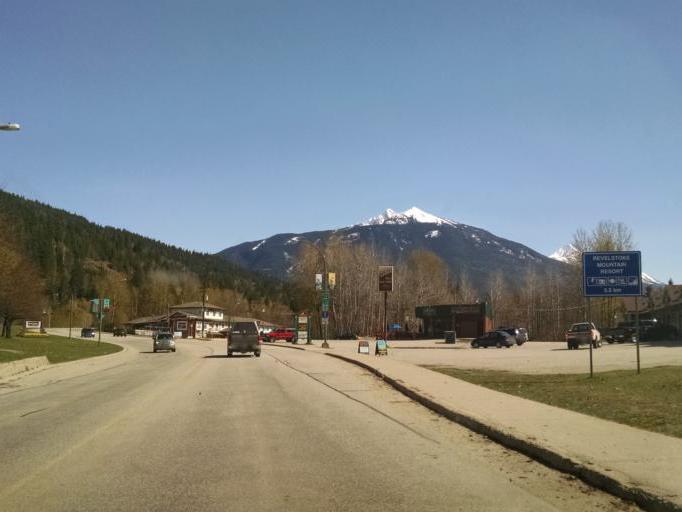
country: CA
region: British Columbia
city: Revelstoke
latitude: 51.0085
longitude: -118.2135
